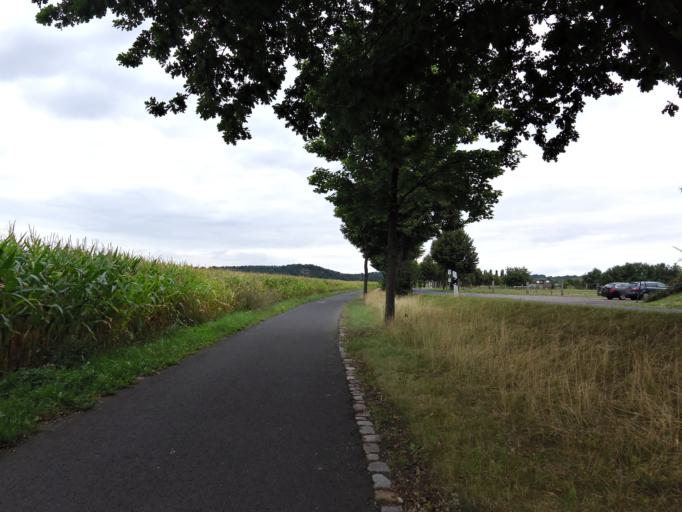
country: DE
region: Saxony
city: Weissig
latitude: 51.2151
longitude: 13.4089
